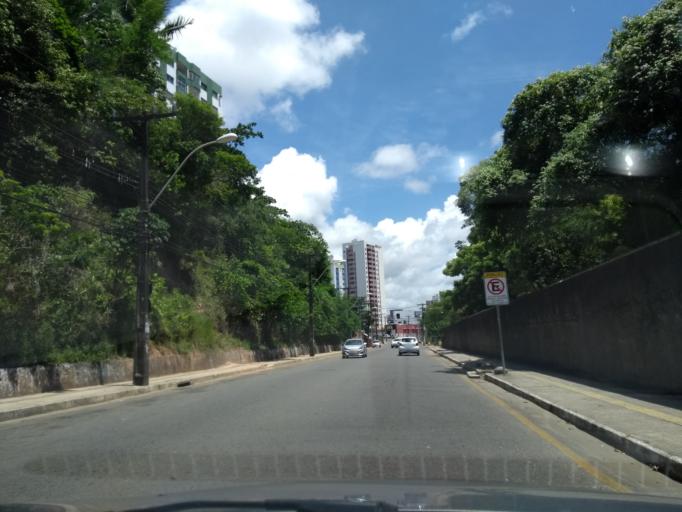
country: BR
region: Bahia
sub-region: Salvador
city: Salvador
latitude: -12.9665
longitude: -38.4347
